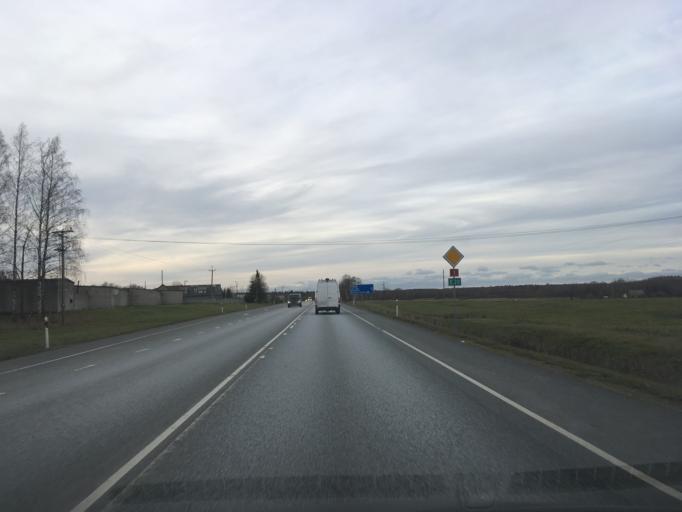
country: EE
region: Ida-Virumaa
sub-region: Kohtla-Jaerve linn
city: Kohtla-Jarve
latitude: 59.4087
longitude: 27.3160
